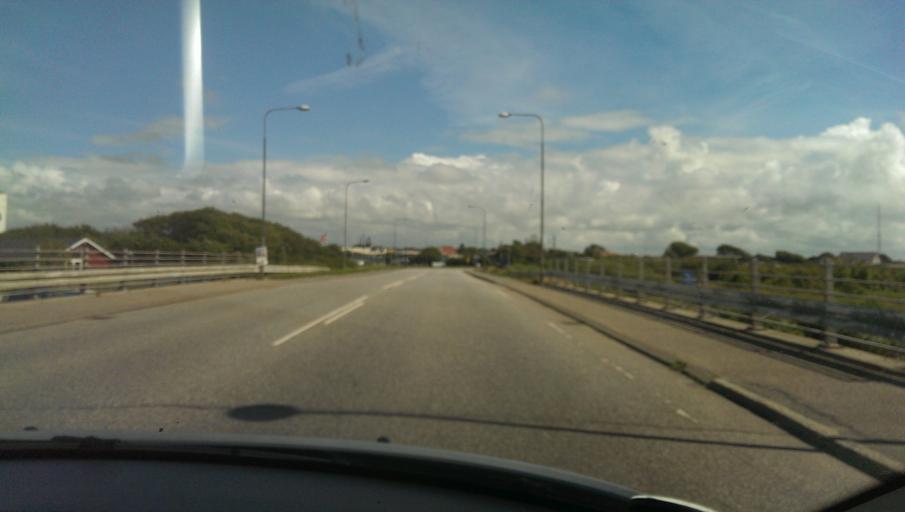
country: DK
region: Central Jutland
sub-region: Ringkobing-Skjern Kommune
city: Ringkobing
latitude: 56.0960
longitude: 8.2320
